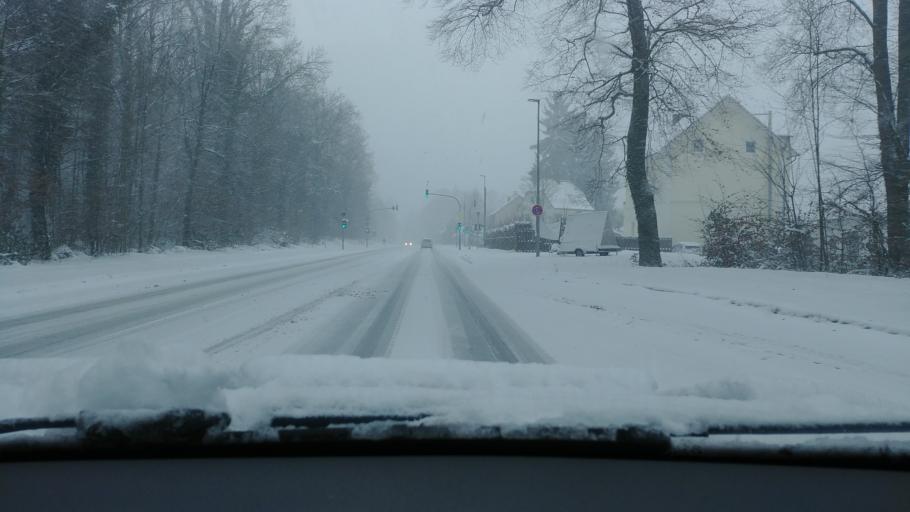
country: DE
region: North Rhine-Westphalia
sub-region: Regierungsbezirk Koln
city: Bergisch Gladbach
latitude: 50.9731
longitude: 7.1440
